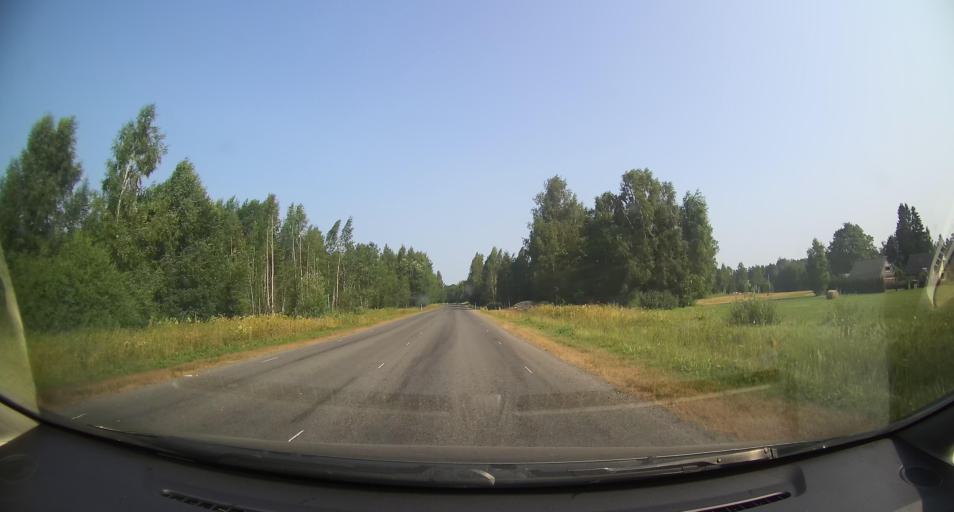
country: EE
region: Paernumaa
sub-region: Audru vald
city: Audru
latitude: 58.4261
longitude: 24.3155
